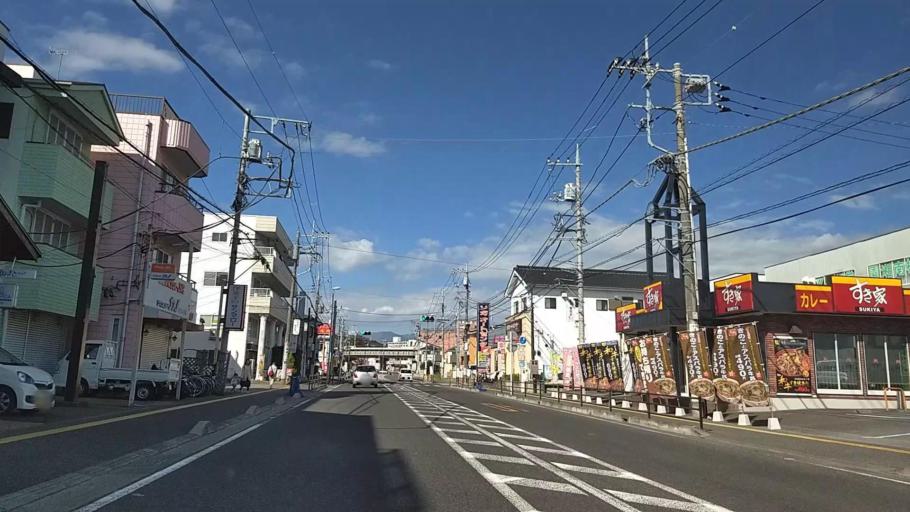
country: JP
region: Kanagawa
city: Ninomiya
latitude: 35.3069
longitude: 139.2535
